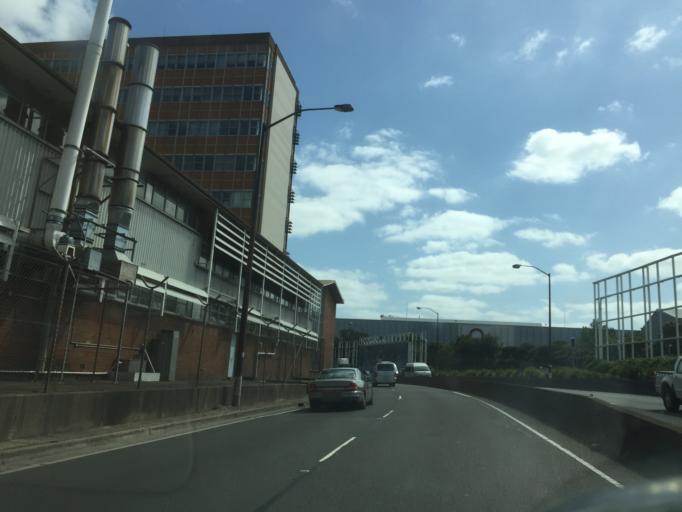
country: AU
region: New South Wales
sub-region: Botany Bay
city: Mascot
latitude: -33.9287
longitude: 151.1838
